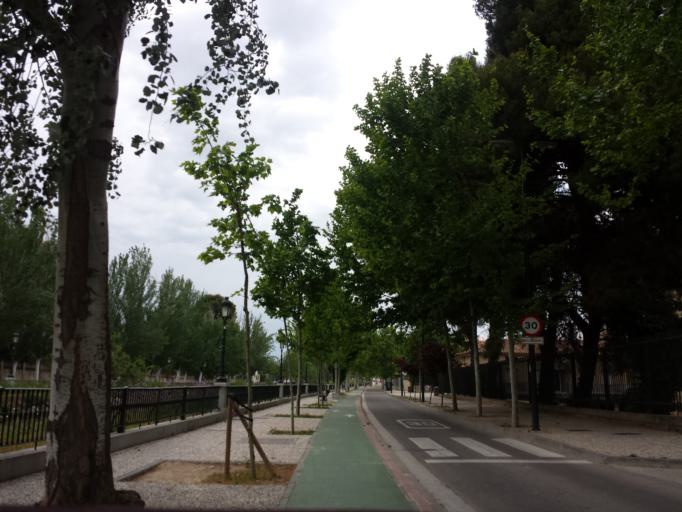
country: ES
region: Aragon
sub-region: Provincia de Zaragoza
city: Delicias
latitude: 41.6252
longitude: -0.9068
